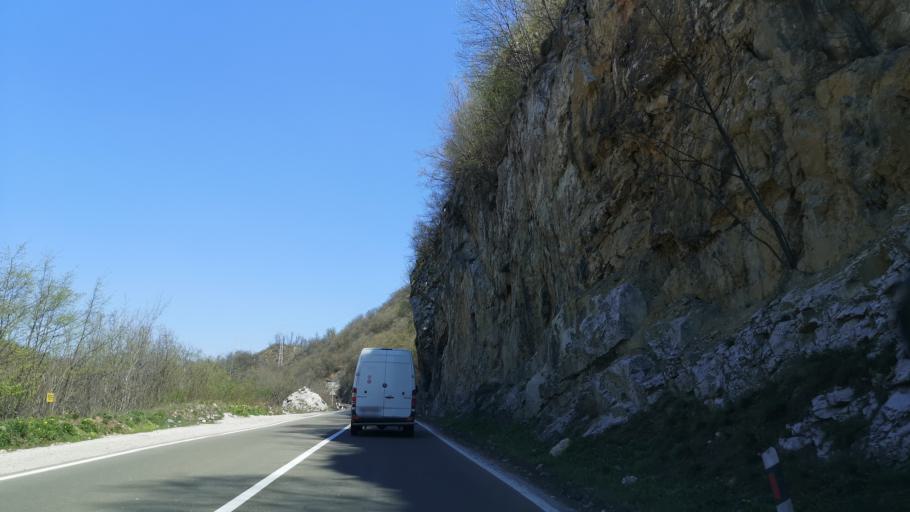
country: RS
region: Central Serbia
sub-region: Moravicki Okrug
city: Lucani
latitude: 43.9082
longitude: 20.2057
